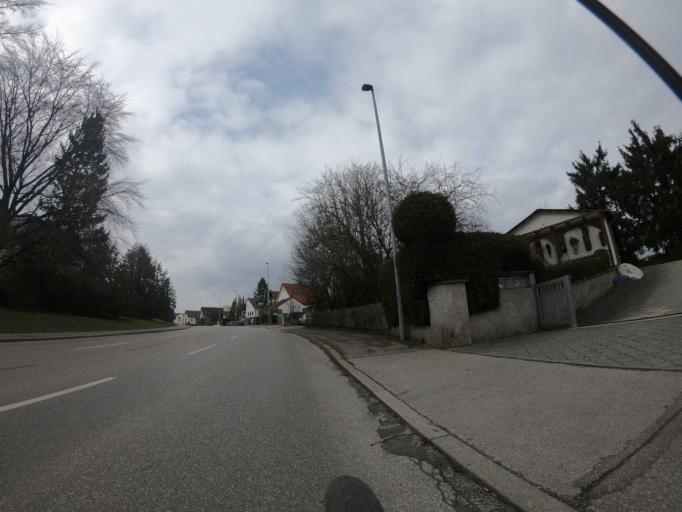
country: DE
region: Bavaria
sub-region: Upper Bavaria
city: Fuerstenfeldbruck
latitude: 48.1716
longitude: 11.2389
